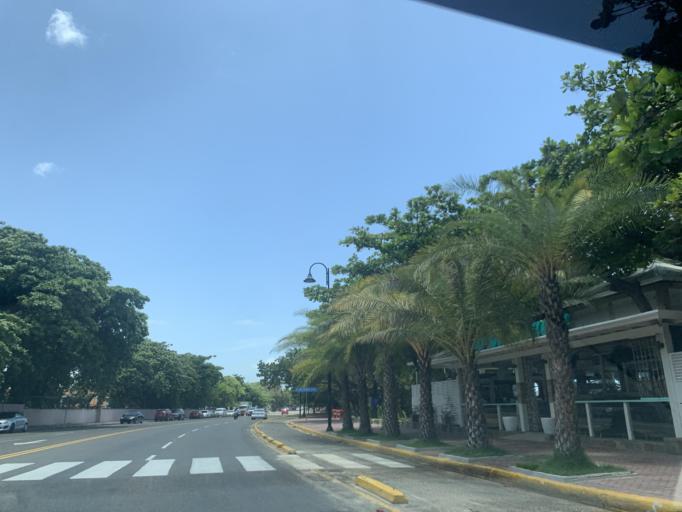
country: DO
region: Puerto Plata
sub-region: Puerto Plata
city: Puerto Plata
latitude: 19.7905
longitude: -70.6718
